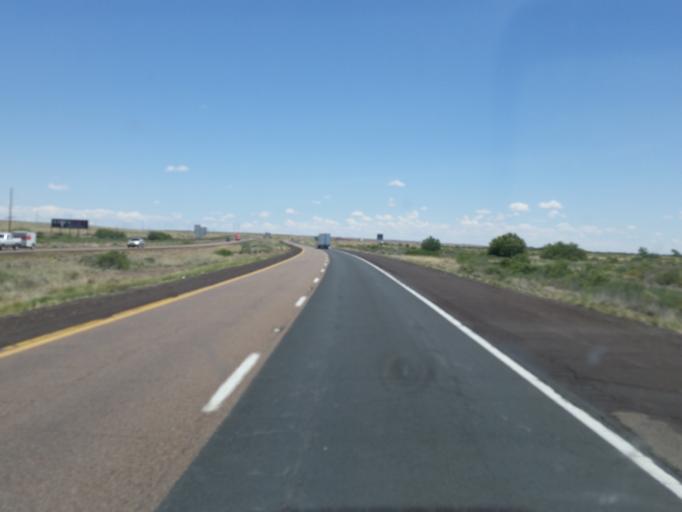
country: US
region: Arizona
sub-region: Navajo County
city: Winslow
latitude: 35.0064
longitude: -110.6298
